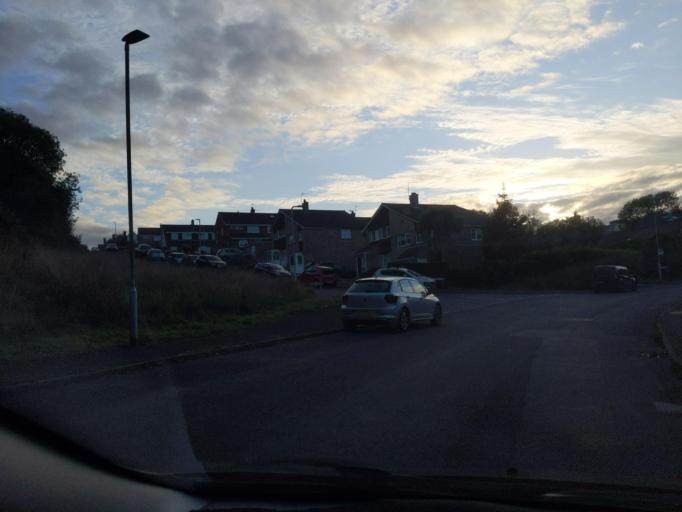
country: GB
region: England
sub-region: Plymouth
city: Plymstock
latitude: 50.3577
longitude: -4.0630
